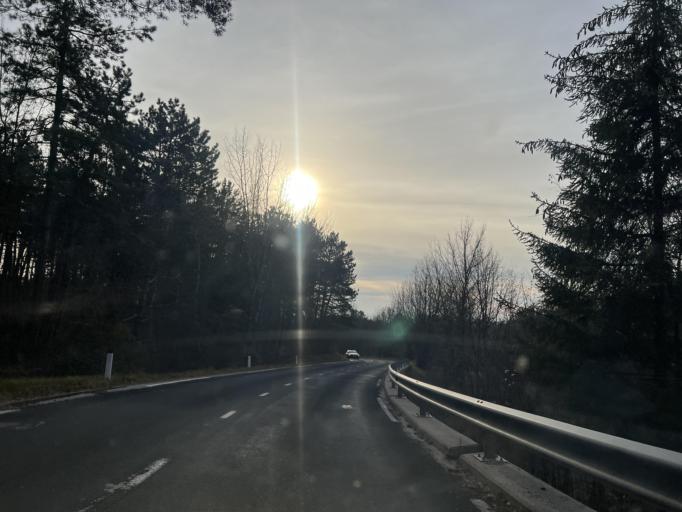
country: SI
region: Nova Gorica
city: Sempas
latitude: 45.9733
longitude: 13.7282
